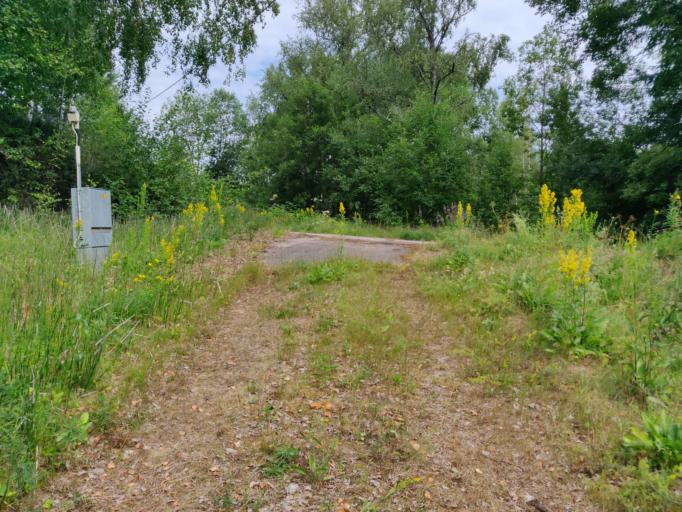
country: SE
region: Vaermland
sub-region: Munkfors Kommun
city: Munkfors
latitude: 59.9566
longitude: 13.5266
